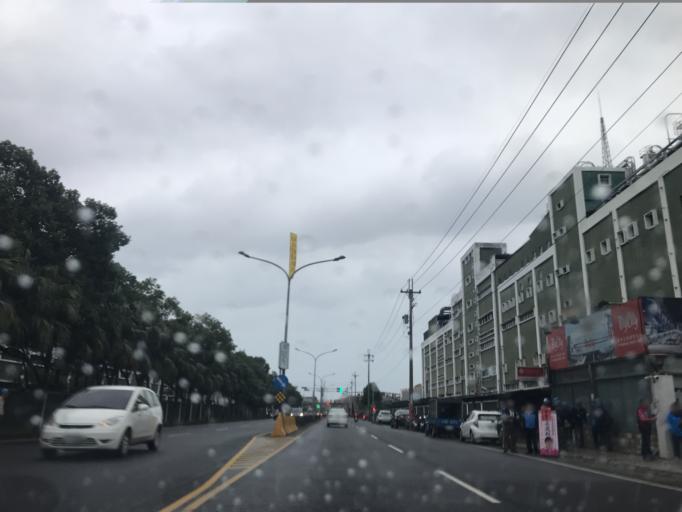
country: TW
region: Taiwan
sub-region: Hsinchu
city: Zhubei
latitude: 24.8255
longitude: 121.0570
